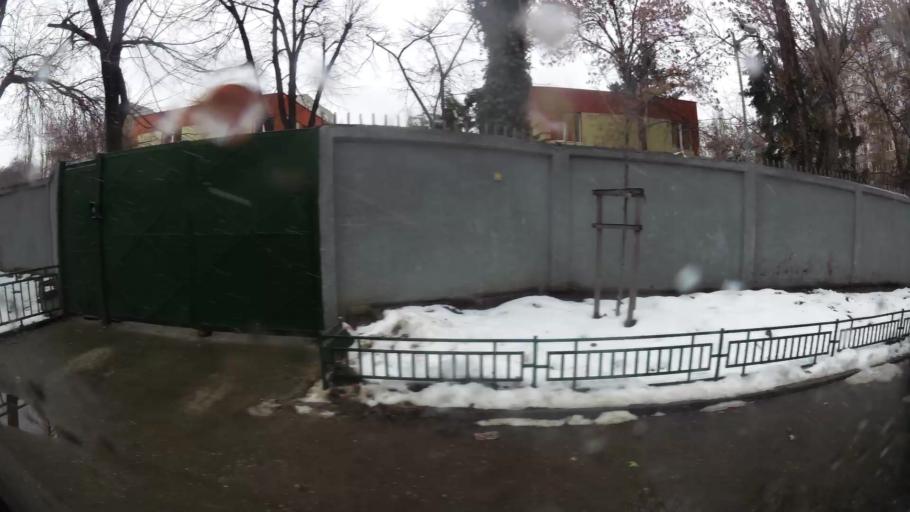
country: RO
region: Ilfov
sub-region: Comuna Chiajna
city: Rosu
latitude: 44.4255
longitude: 26.0400
